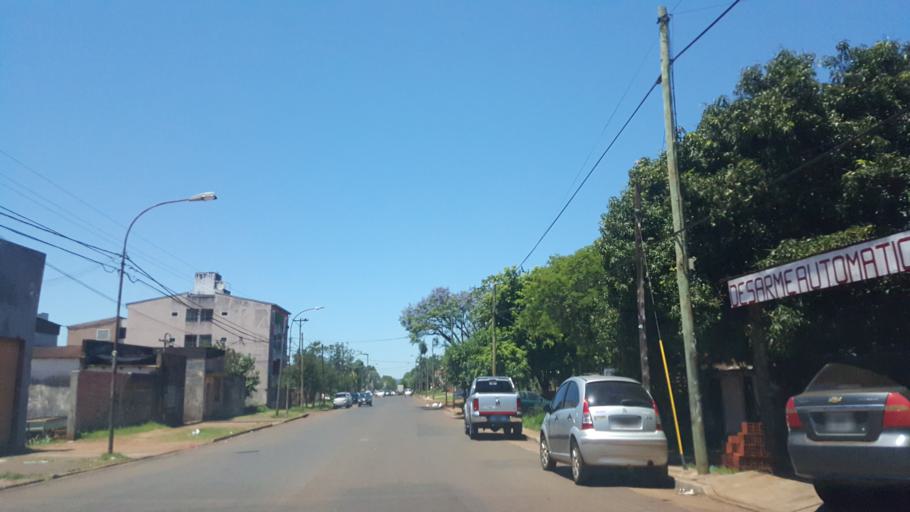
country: AR
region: Misiones
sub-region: Departamento de Capital
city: Posadas
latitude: -27.3831
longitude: -55.9111
